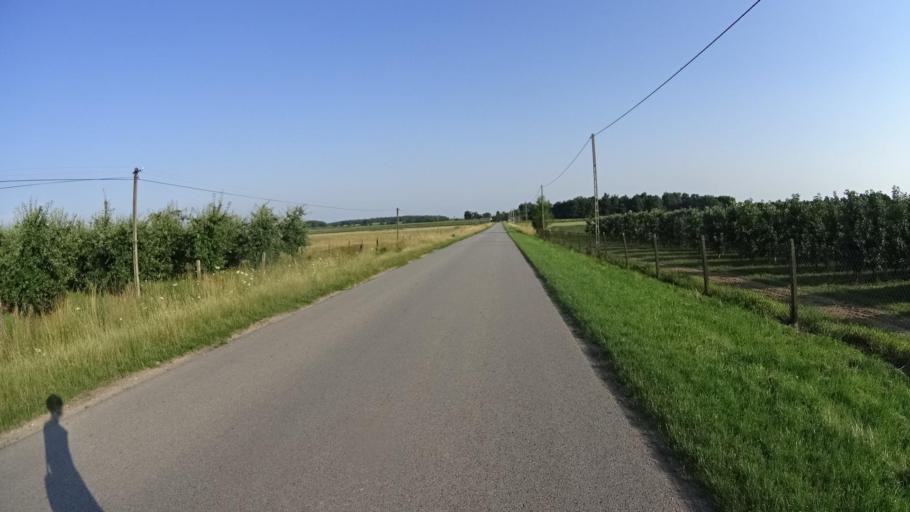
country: PL
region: Masovian Voivodeship
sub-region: Powiat grojecki
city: Goszczyn
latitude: 51.7132
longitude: 20.8520
